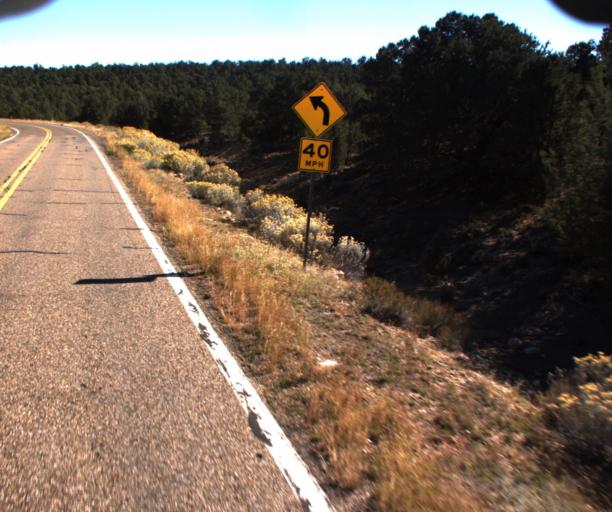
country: US
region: Arizona
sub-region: Coconino County
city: Fredonia
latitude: 36.7408
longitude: -112.1079
